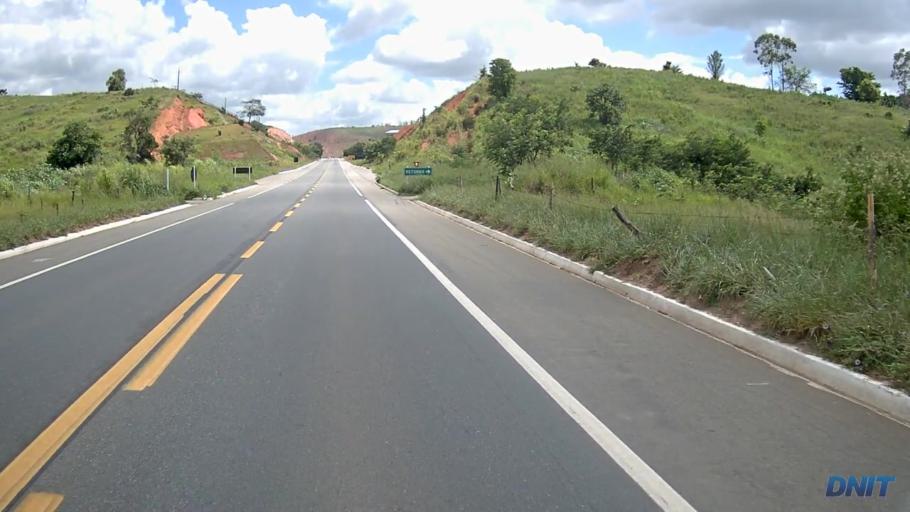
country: BR
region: Minas Gerais
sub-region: Governador Valadares
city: Governador Valadares
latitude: -18.9020
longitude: -42.0036
